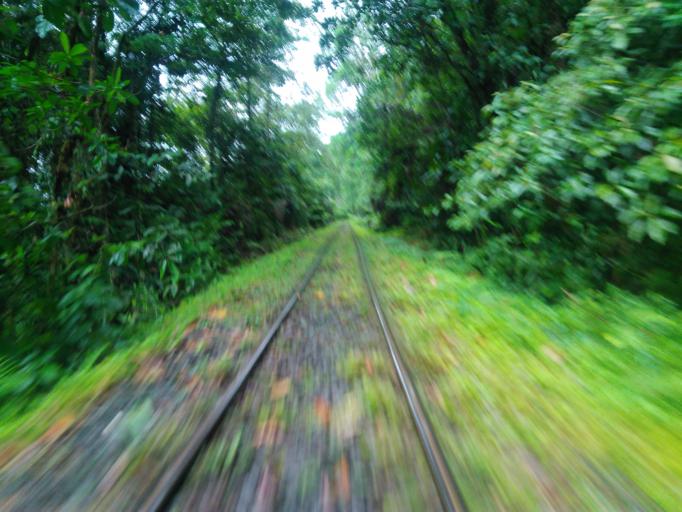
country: CO
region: Valle del Cauca
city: Buenaventura
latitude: 3.8481
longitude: -76.8858
